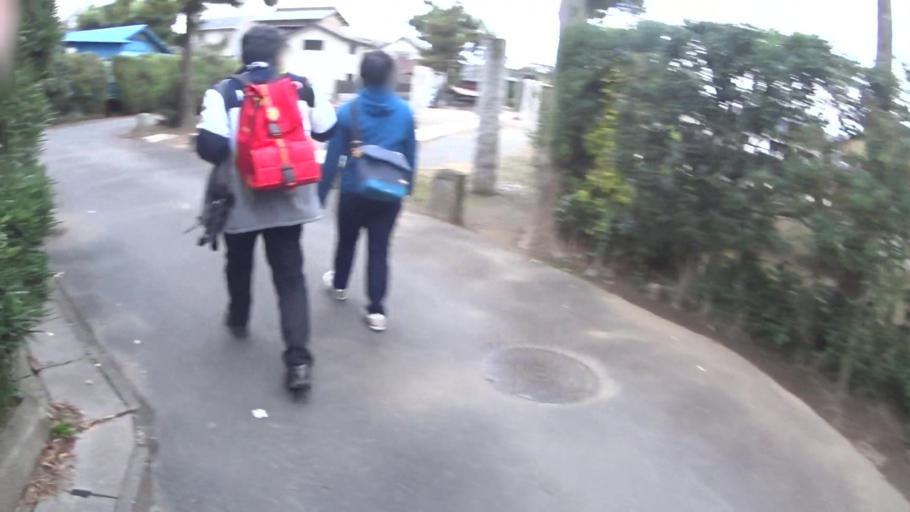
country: JP
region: Saitama
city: Yashio-shi
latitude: 35.8353
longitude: 139.8473
